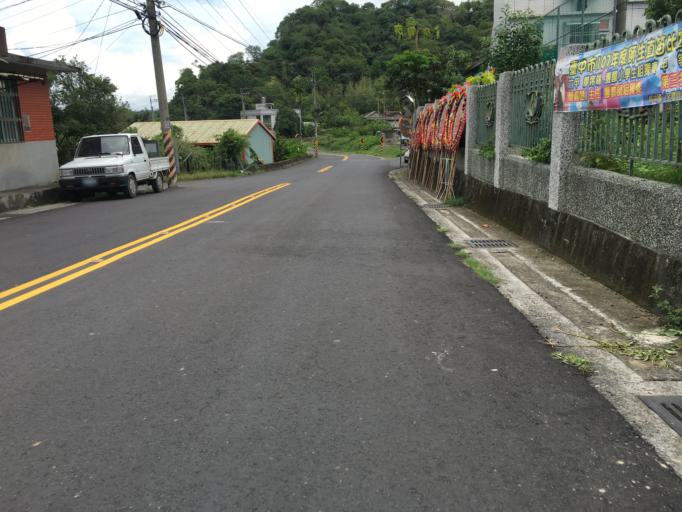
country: TW
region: Taiwan
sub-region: Taichung City
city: Taichung
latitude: 24.0660
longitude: 120.7355
